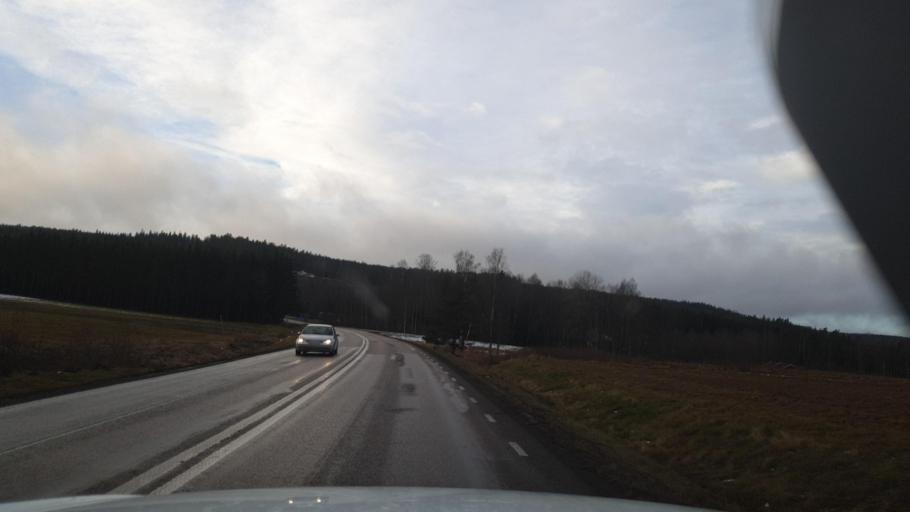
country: SE
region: Vaermland
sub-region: Eda Kommun
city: Amotfors
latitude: 59.6806
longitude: 12.3927
